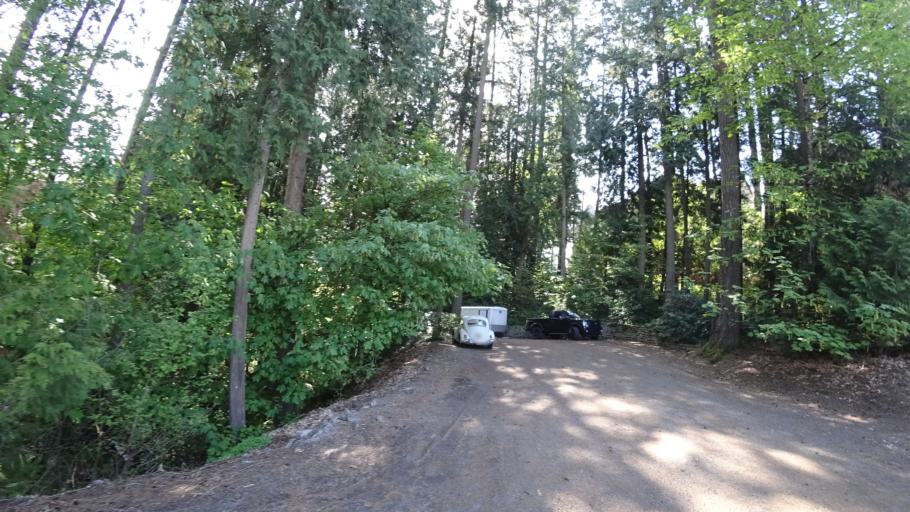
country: US
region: Oregon
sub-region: Washington County
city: Aloha
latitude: 45.4520
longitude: -122.8466
